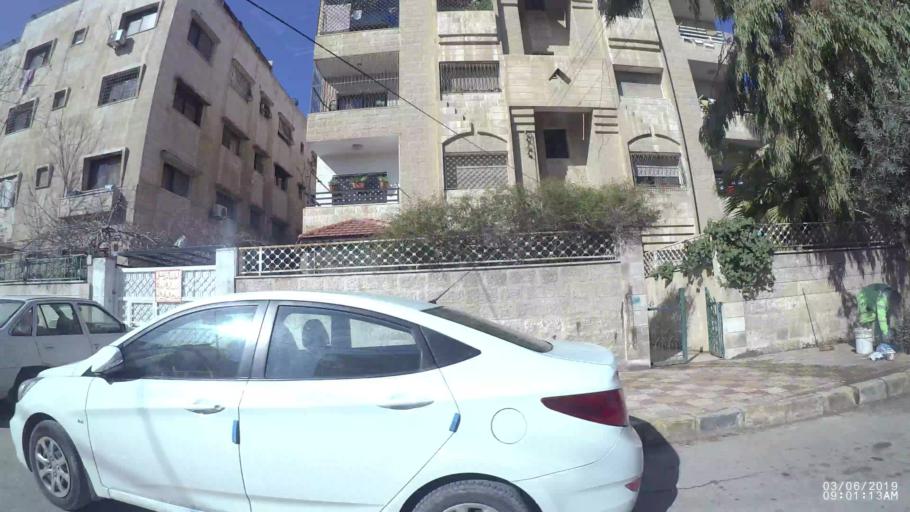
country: JO
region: Amman
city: Amman
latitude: 31.9852
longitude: 35.9924
